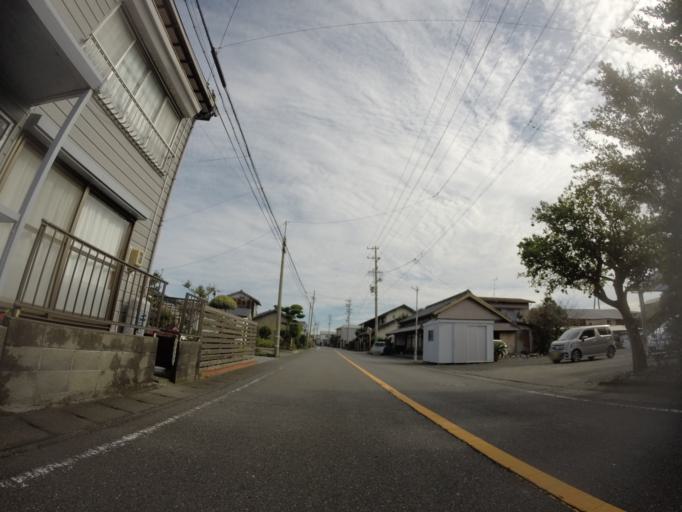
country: JP
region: Shizuoka
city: Sagara
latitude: 34.7546
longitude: 138.2491
